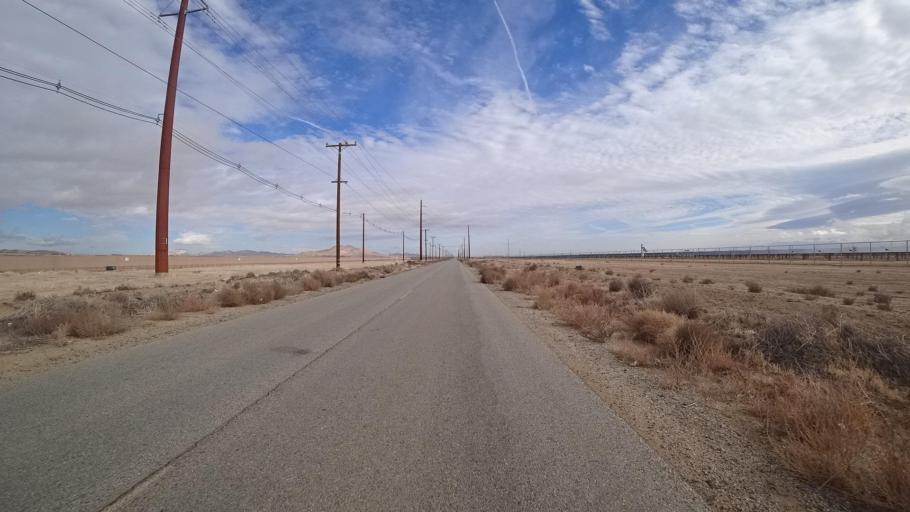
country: US
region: California
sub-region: Kern County
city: Rosamond
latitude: 34.8632
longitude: -118.3501
